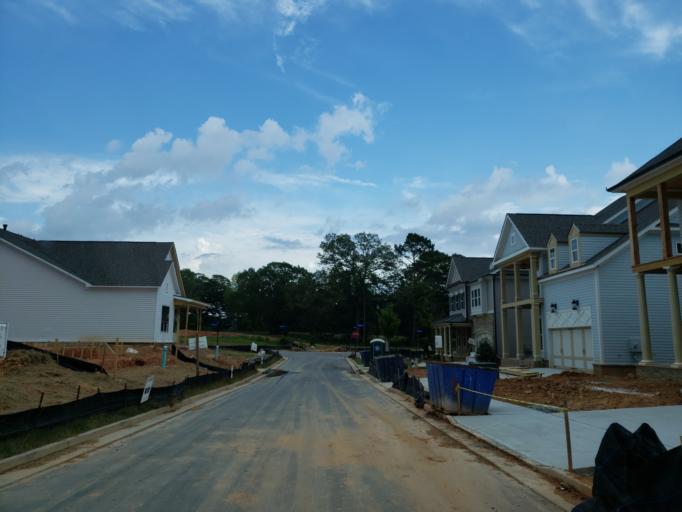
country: US
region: Georgia
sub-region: Cherokee County
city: Holly Springs
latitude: 34.1790
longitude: -84.4357
